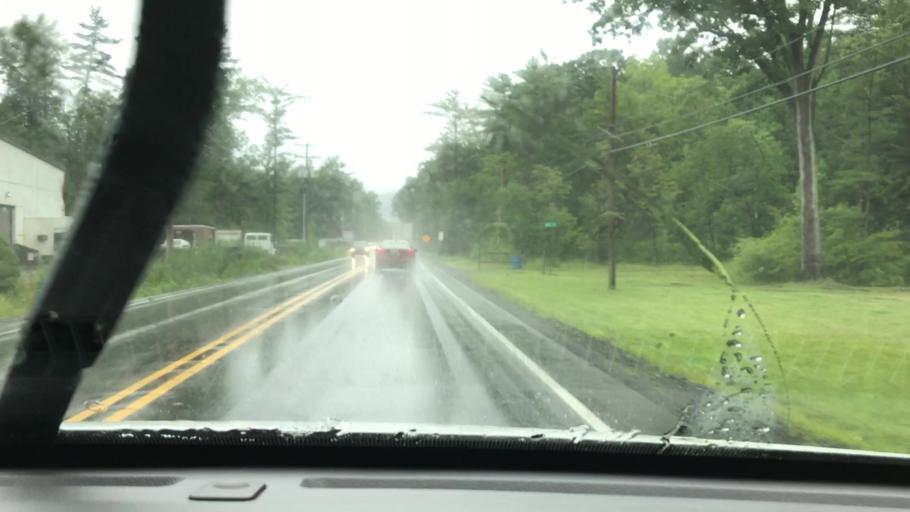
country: US
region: Pennsylvania
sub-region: Blair County
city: Tyrone
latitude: 40.7282
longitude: -78.1892
